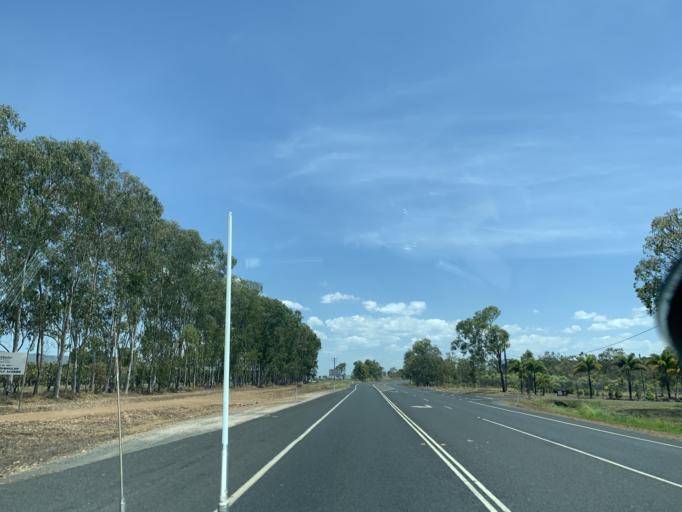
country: AU
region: Queensland
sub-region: Tablelands
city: Mareeba
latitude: -16.9783
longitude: 145.5322
